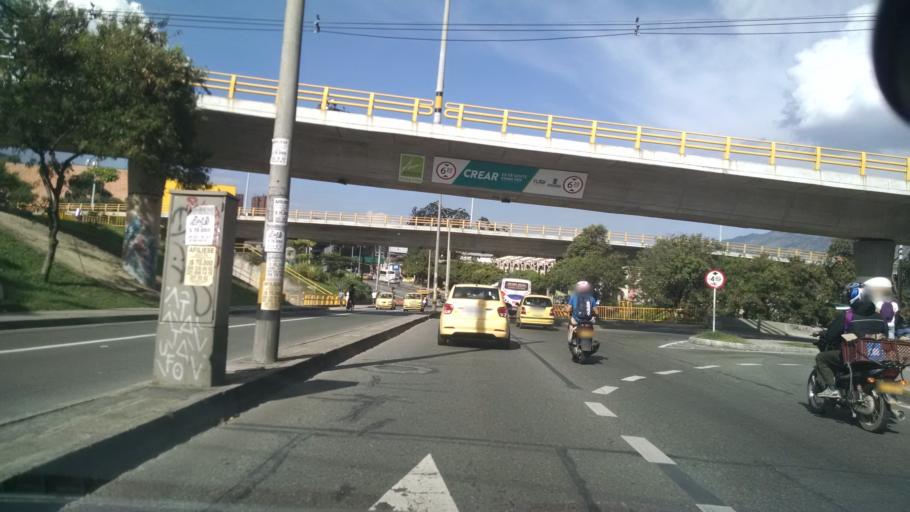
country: CO
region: Antioquia
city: Medellin
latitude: 6.2714
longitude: -75.5945
